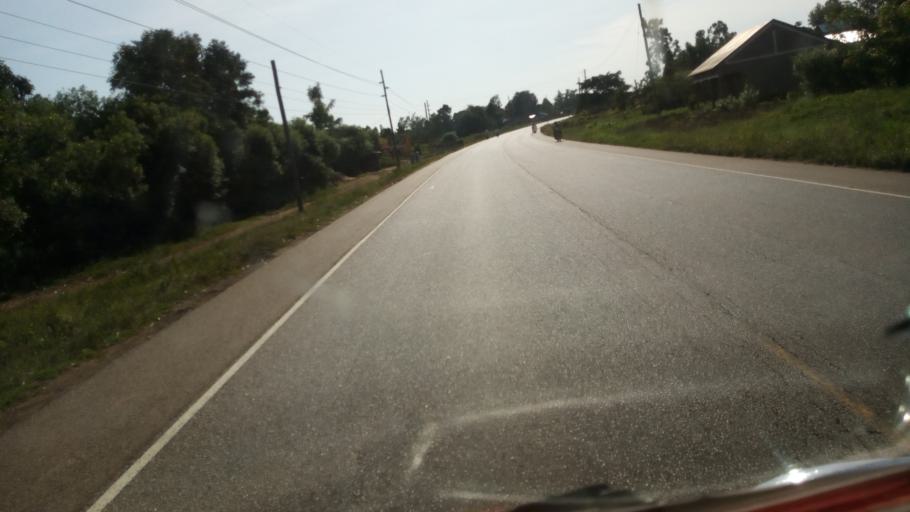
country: UG
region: Eastern Region
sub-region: Bugiri District
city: Bugiri
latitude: 0.5128
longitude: 33.8090
